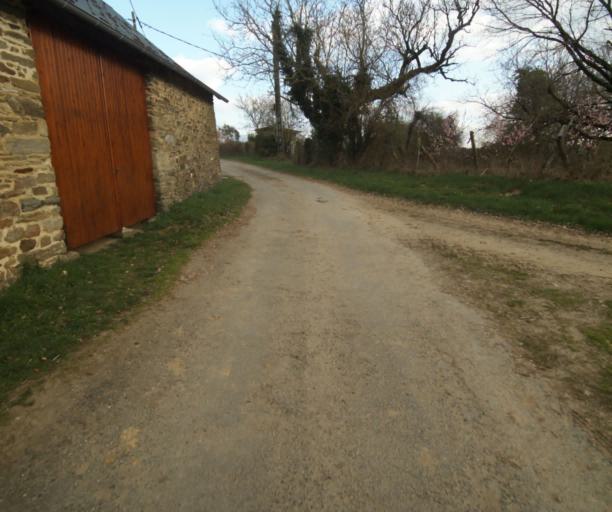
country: FR
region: Limousin
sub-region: Departement de la Correze
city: Saint-Clement
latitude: 45.3657
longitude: 1.6303
